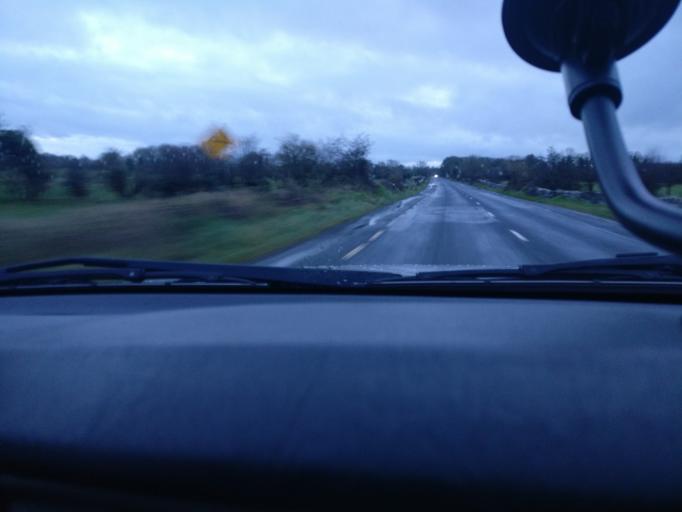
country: IE
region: Connaught
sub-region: County Galway
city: Loughrea
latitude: 53.2539
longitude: -8.4408
